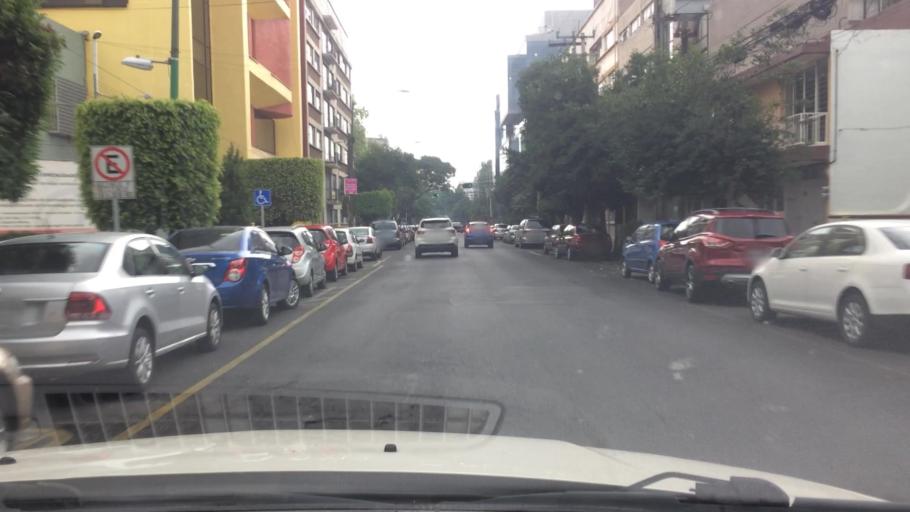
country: MX
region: Mexico City
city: Colonia del Valle
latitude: 19.3717
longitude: -99.1743
